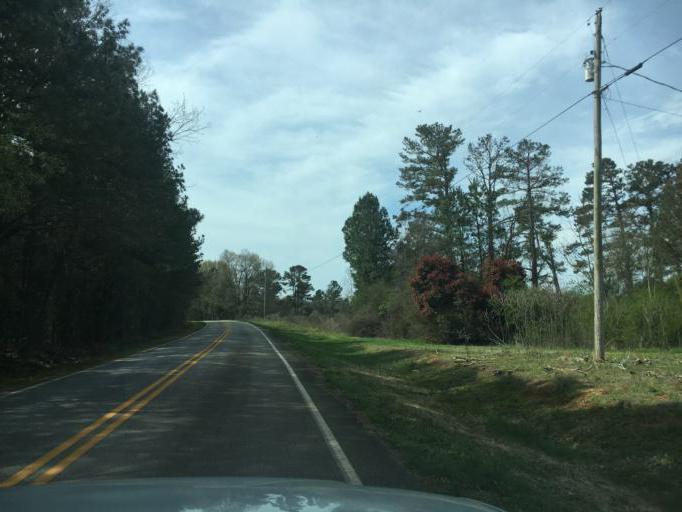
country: US
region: Georgia
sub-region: Franklin County
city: Lavonia
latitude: 34.4198
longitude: -83.0562
